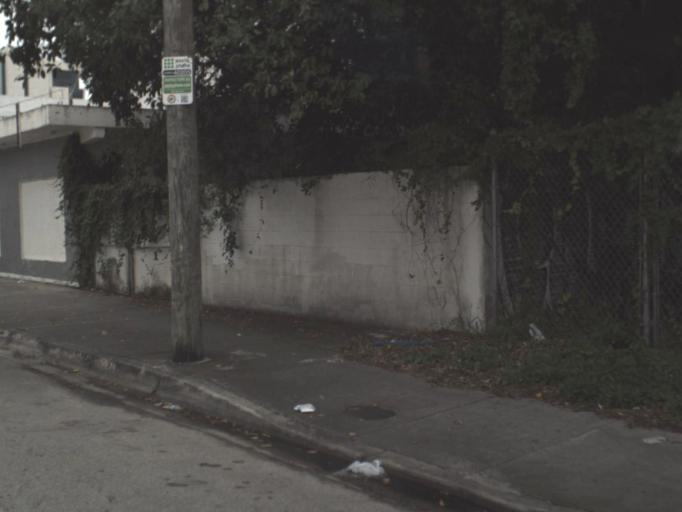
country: US
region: Florida
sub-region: Miami-Dade County
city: Miami
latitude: 25.7787
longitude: -80.2017
